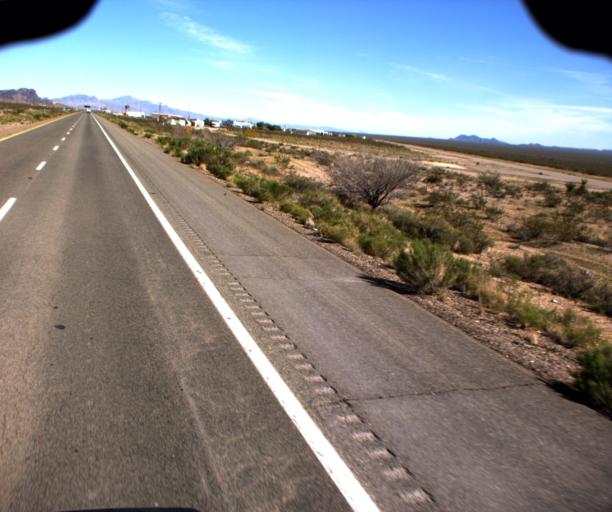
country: US
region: Arizona
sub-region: Mohave County
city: Dolan Springs
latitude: 35.7084
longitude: -114.4789
